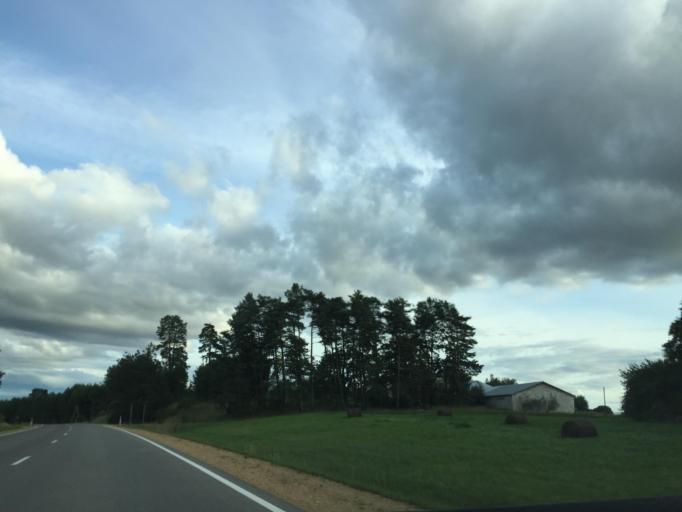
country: LV
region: Nereta
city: Nereta
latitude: 56.2253
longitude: 25.2797
